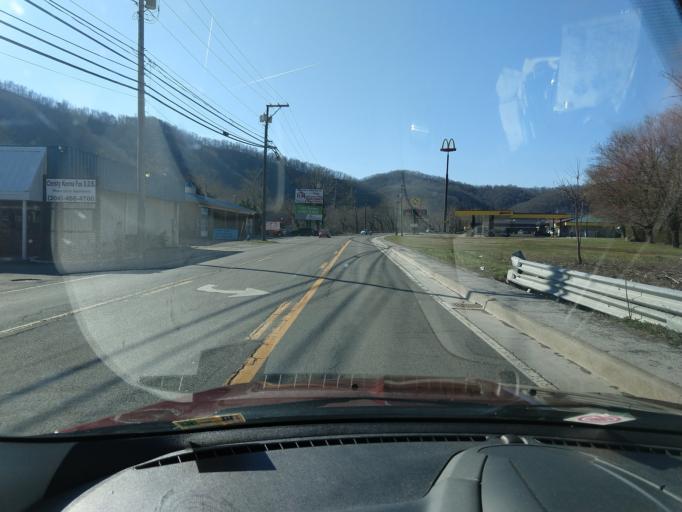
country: US
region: West Virginia
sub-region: Summers County
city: Hinton
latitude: 37.6556
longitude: -80.8860
